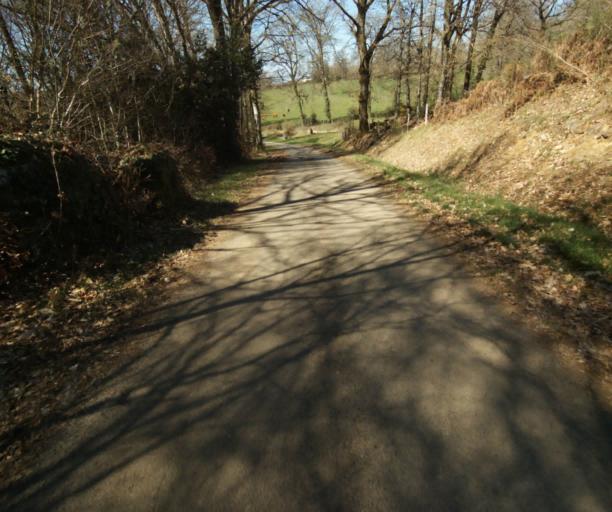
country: FR
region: Limousin
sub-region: Departement de la Correze
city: Saint-Clement
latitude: 45.3716
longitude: 1.6809
